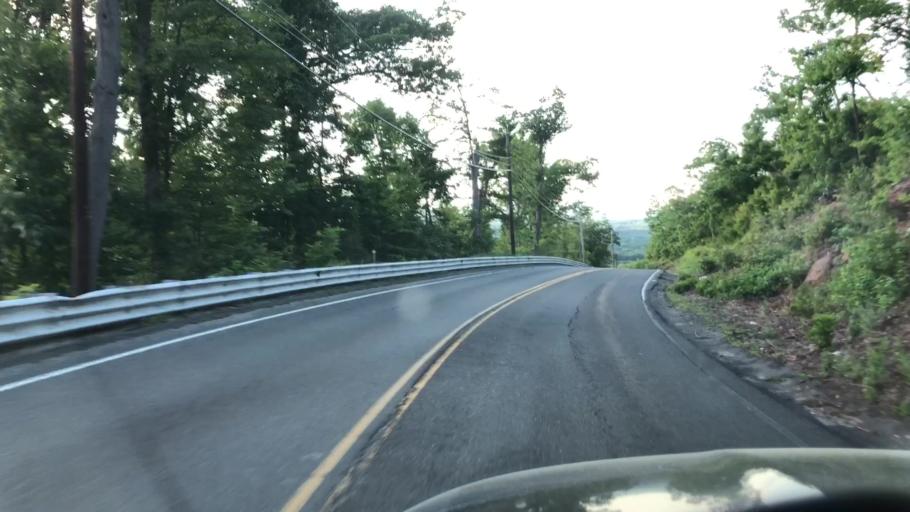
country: US
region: Massachusetts
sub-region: Hampshire County
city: Easthampton
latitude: 42.2397
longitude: -72.6527
